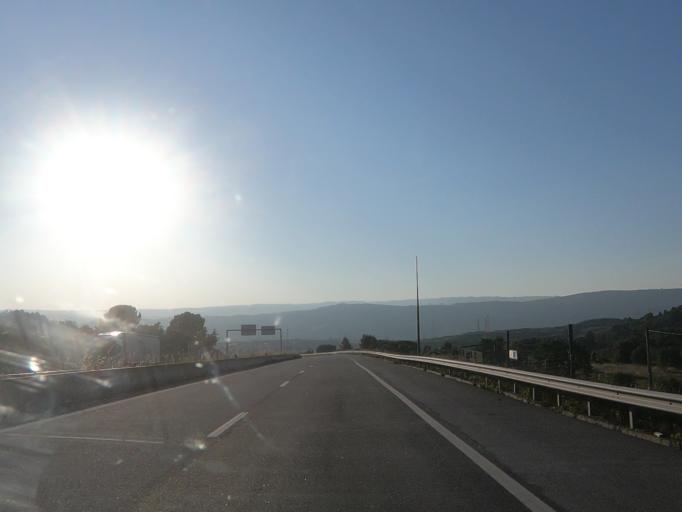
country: PT
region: Guarda
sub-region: Celorico da Beira
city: Celorico da Beira
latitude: 40.6268
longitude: -7.4052
